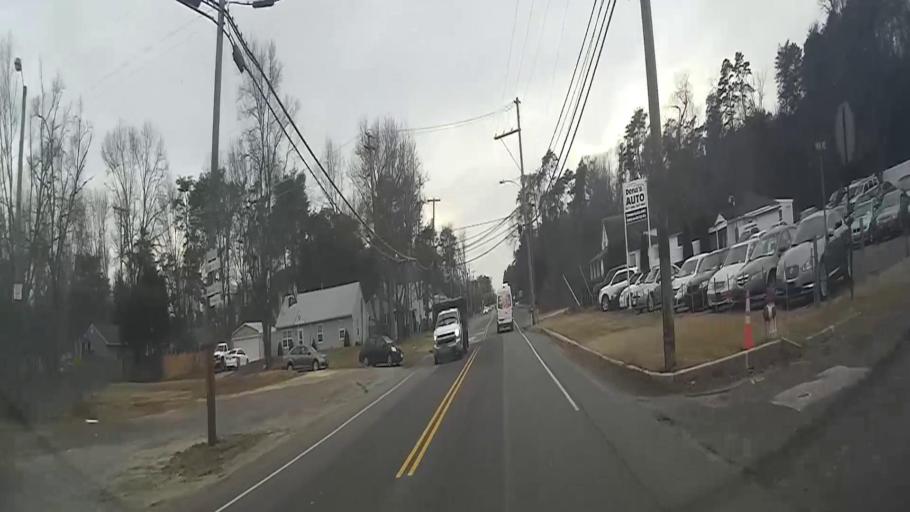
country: US
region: New Jersey
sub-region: Camden County
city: Berlin
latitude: 39.7780
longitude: -74.9557
